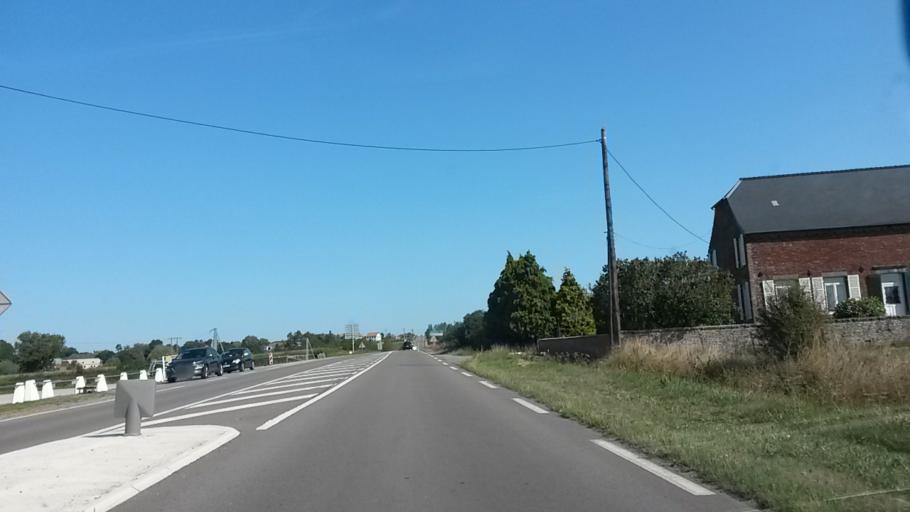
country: FR
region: Nord-Pas-de-Calais
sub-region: Departement du Nord
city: Avesnes-sur-Helpe
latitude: 50.0691
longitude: 3.9287
